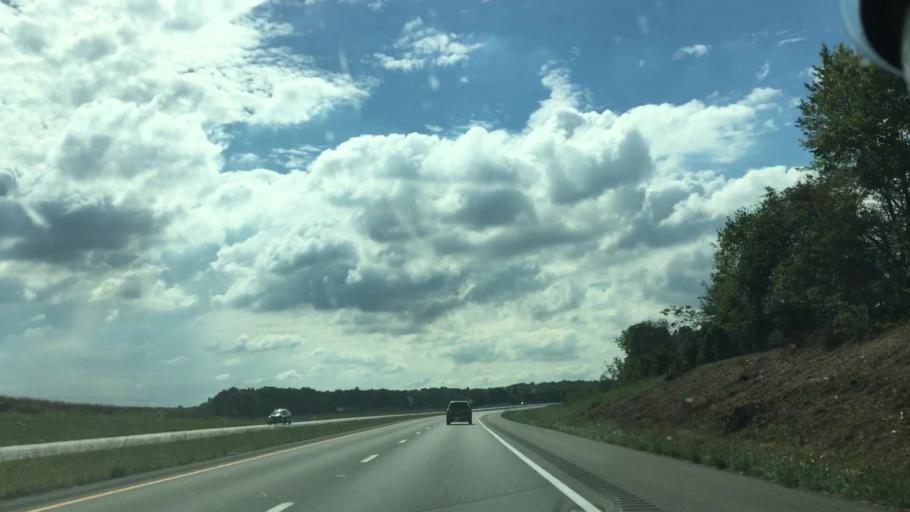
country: US
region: Kentucky
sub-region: Webster County
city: Sebree
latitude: 37.5758
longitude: -87.4811
